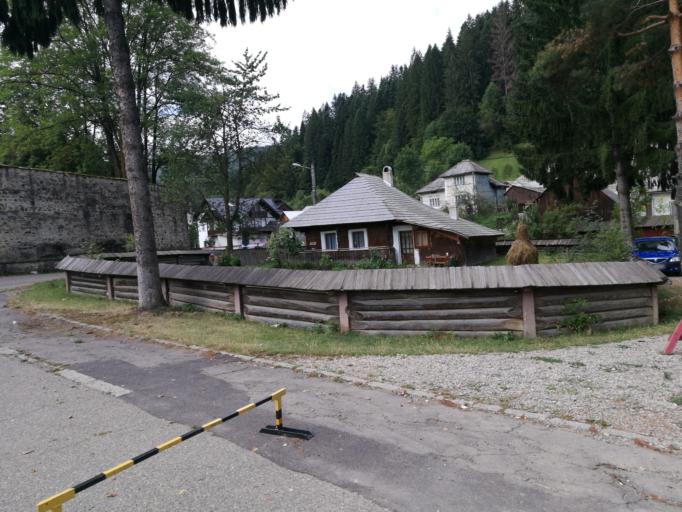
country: RO
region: Suceava
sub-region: Oras Gura Humorului
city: Gura Humorului
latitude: 47.5177
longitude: 25.8643
